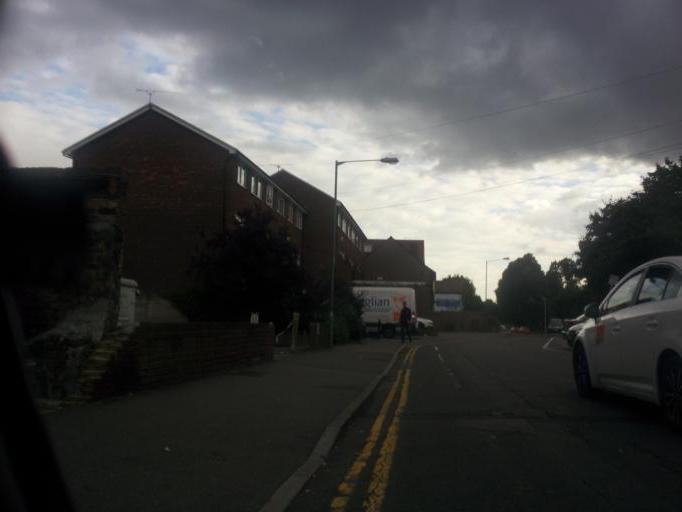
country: GB
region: England
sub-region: Kent
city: Gillingham
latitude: 51.3890
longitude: 0.5424
